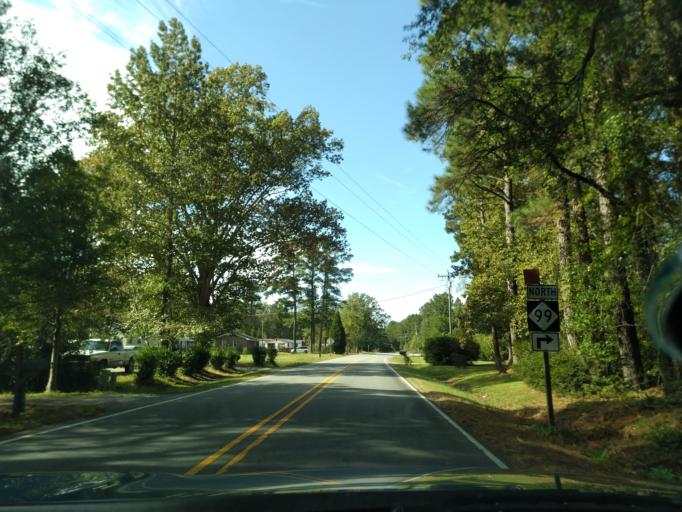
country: US
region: North Carolina
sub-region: Beaufort County
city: Belhaven
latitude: 35.5930
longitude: -76.6657
